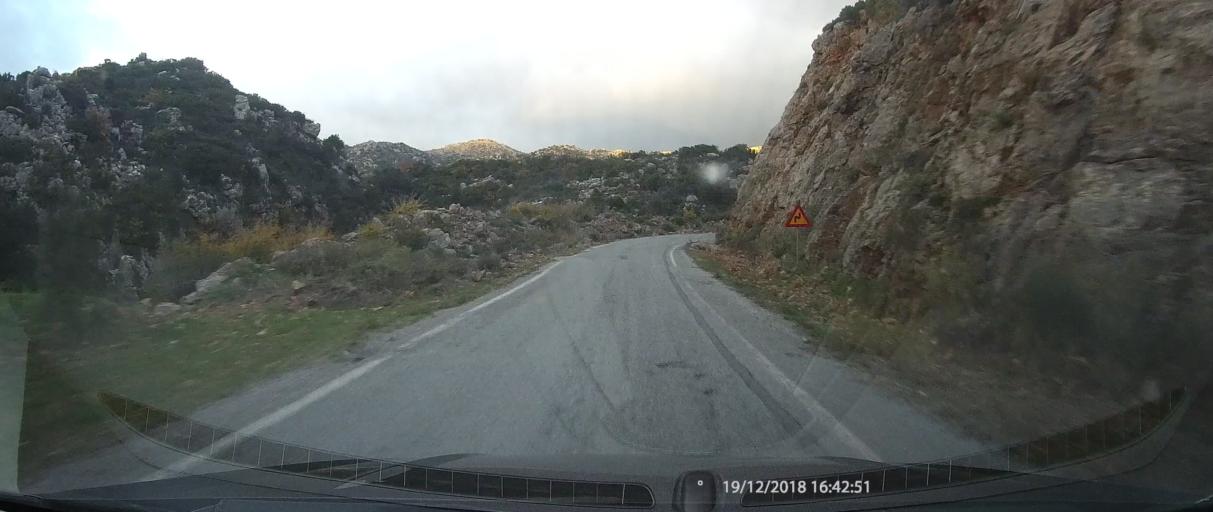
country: GR
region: Peloponnese
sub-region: Nomos Lakonias
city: Sykea
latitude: 36.9091
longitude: 22.9960
